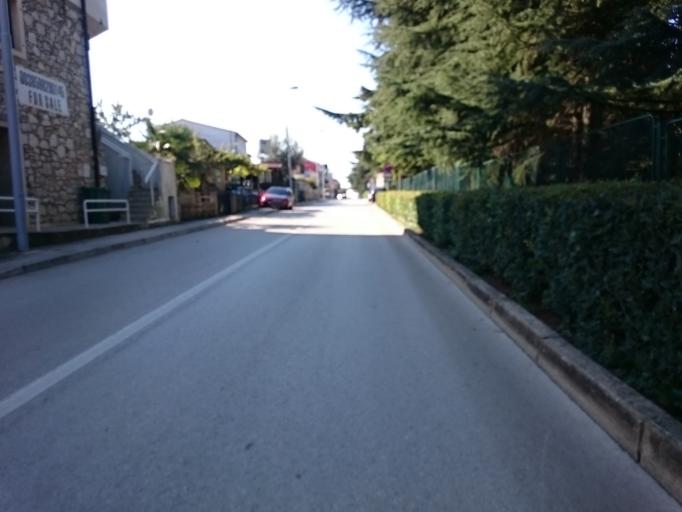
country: HR
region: Istarska
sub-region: Grad Porec
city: Porec
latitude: 45.2421
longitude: 13.6023
